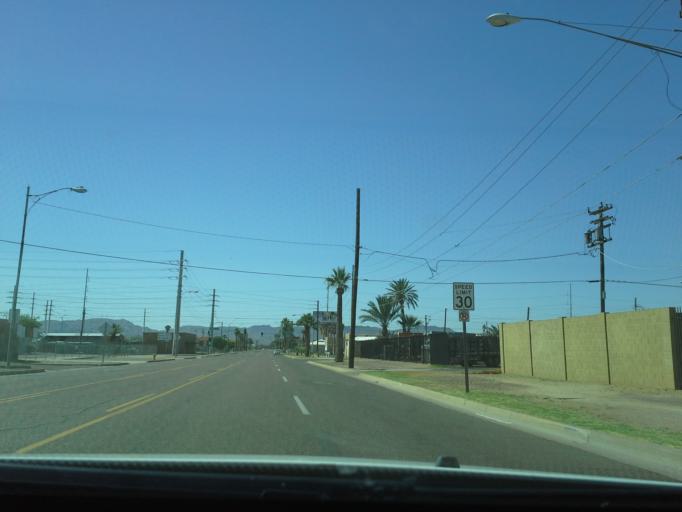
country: US
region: Arizona
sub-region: Maricopa County
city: Phoenix
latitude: 33.4432
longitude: -112.0958
